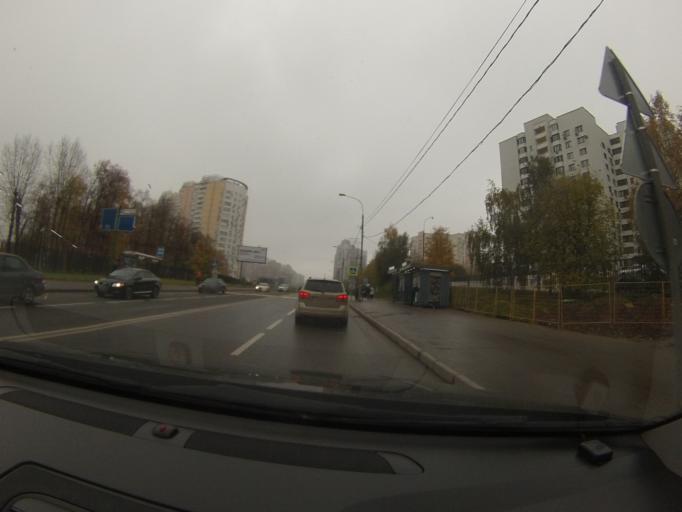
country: RU
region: Moscow
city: Nikol'skoye
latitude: 55.6871
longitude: 37.4872
